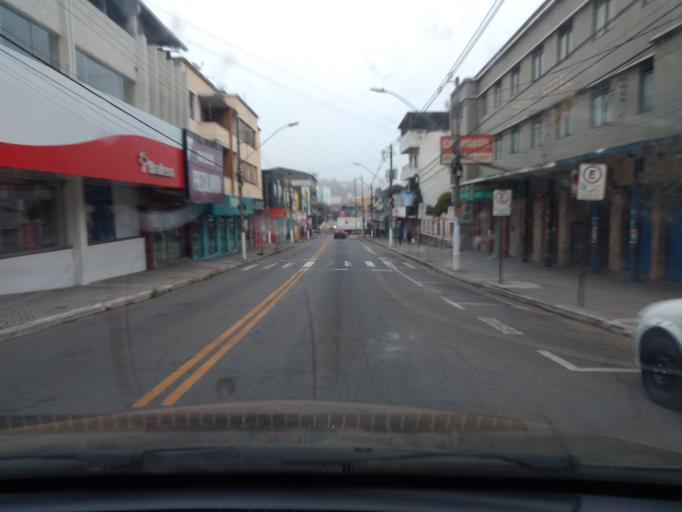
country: BR
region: Minas Gerais
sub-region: Tres Coracoes
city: Tres Coracoes
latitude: -21.6989
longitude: -45.2574
